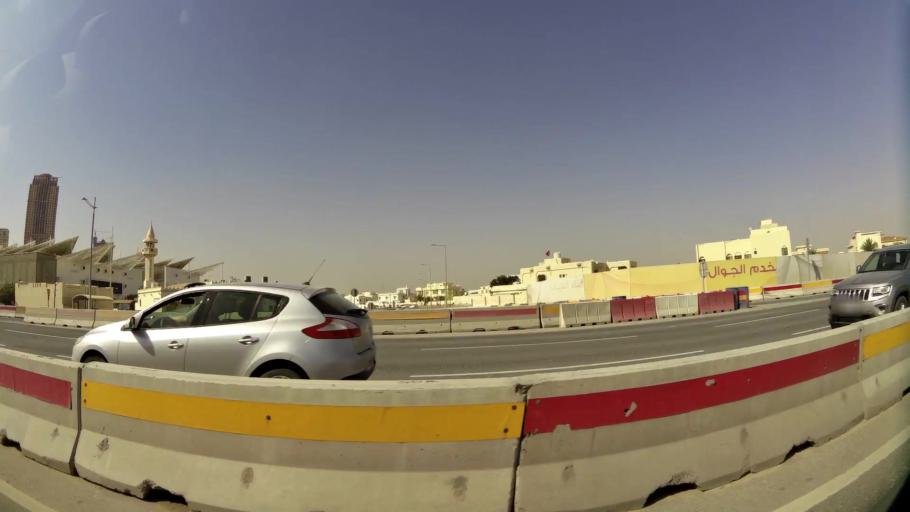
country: QA
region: Baladiyat ad Dawhah
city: Doha
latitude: 25.3313
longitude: 51.5217
